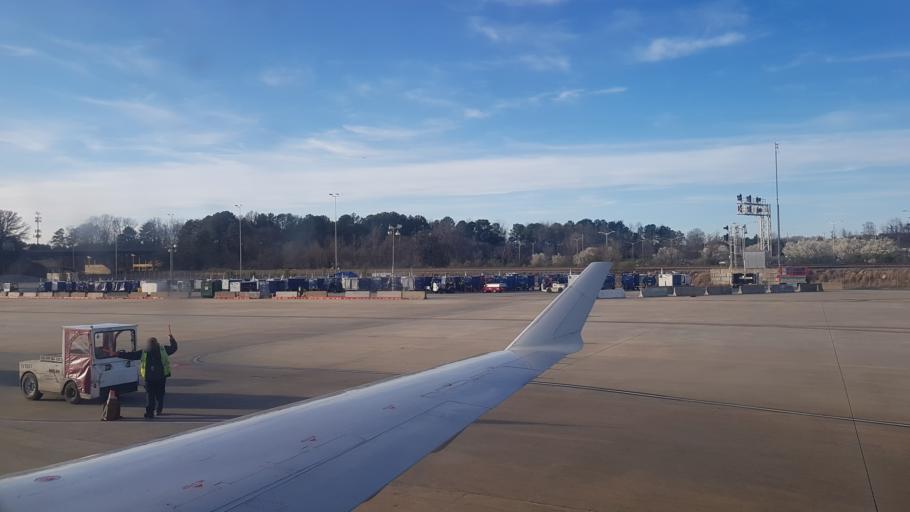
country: US
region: North Carolina
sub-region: Mecklenburg County
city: Charlotte
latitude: 35.2261
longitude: -80.9397
